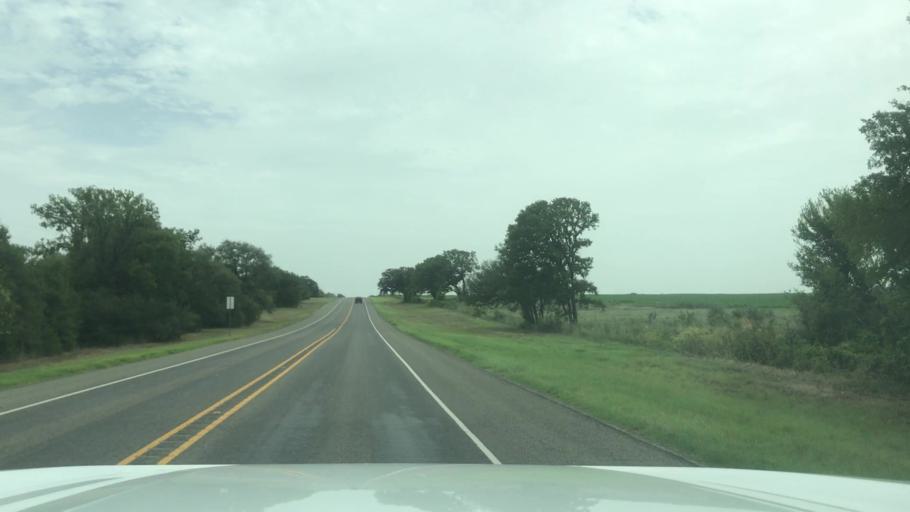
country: US
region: Texas
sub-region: Hamilton County
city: Hico
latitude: 31.9814
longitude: -98.0061
